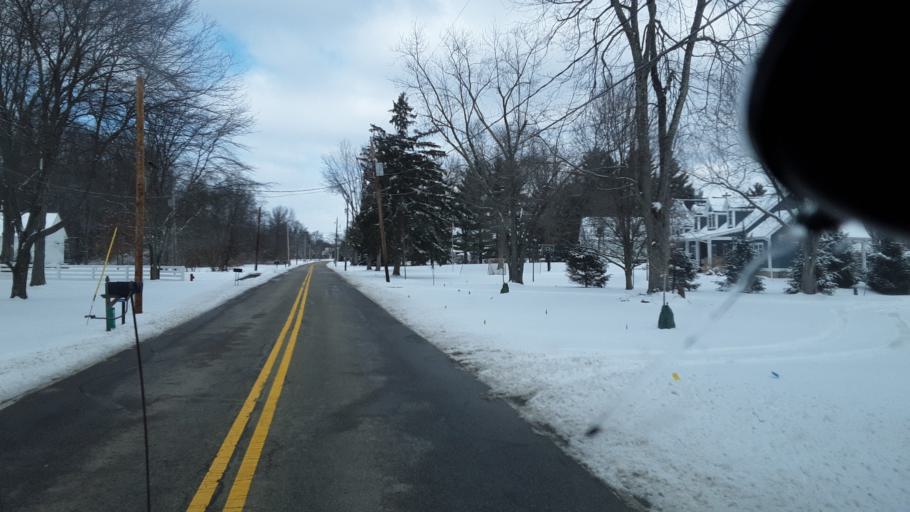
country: US
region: Ohio
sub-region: Franklin County
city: New Albany
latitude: 40.0767
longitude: -82.8321
